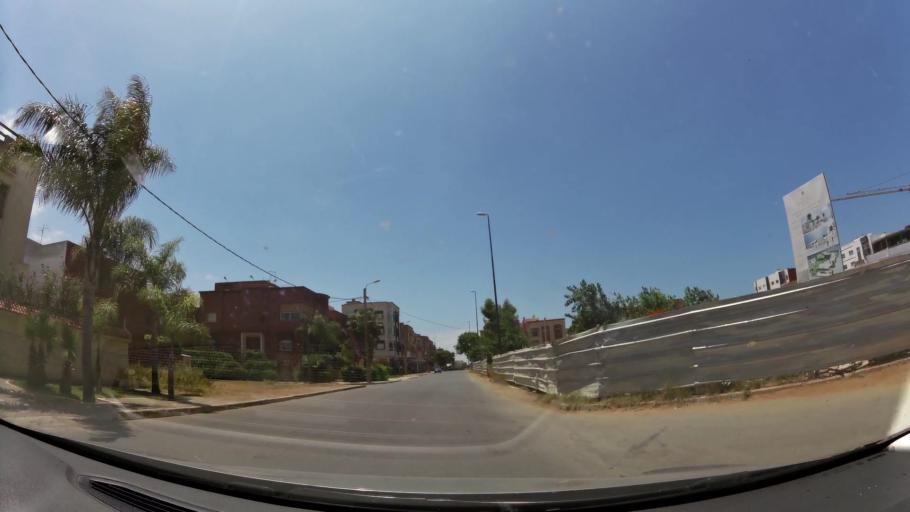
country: MA
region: Gharb-Chrarda-Beni Hssen
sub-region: Kenitra Province
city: Kenitra
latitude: 34.2645
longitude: -6.6230
